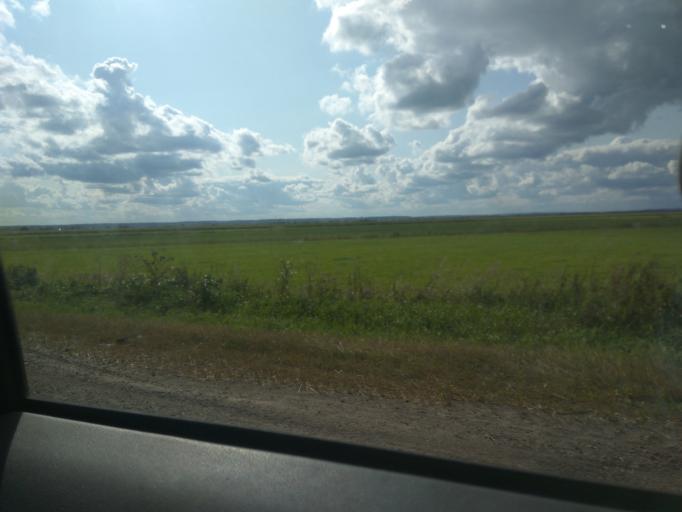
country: RU
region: Moskovskaya
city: Ramenskoye
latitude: 55.5213
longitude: 38.2764
